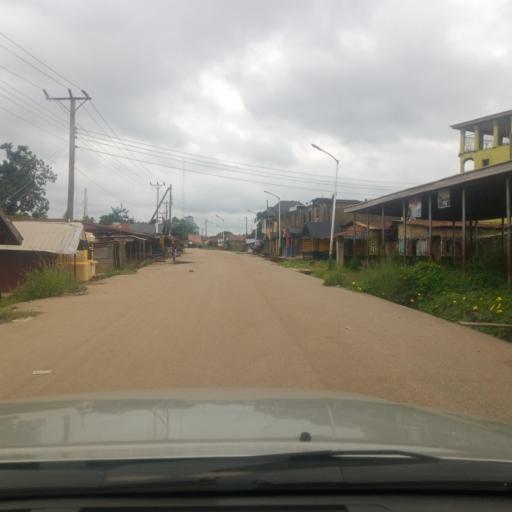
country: NG
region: Ebonyi
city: Effium
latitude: 6.6302
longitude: 8.0565
